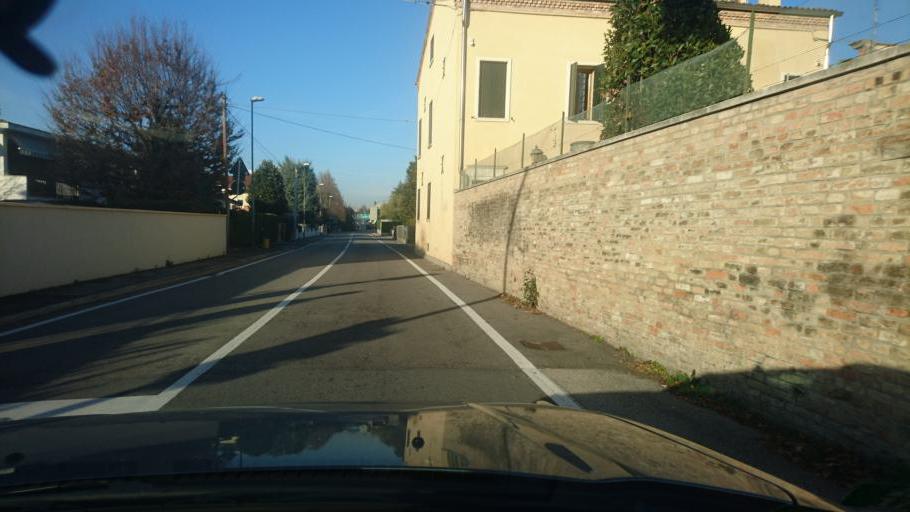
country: IT
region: Veneto
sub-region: Provincia di Padova
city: Noventa
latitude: 45.4163
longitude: 11.9473
